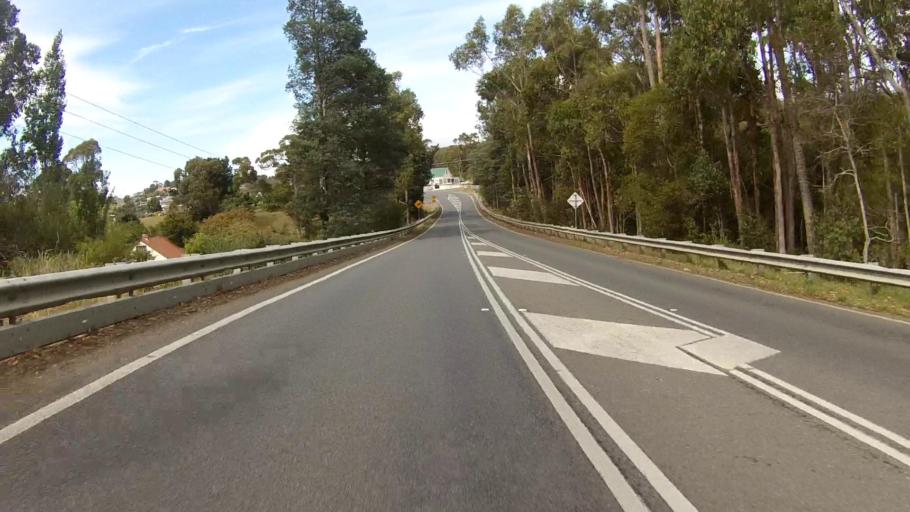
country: AU
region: Tasmania
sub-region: Kingborough
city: Kettering
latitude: -43.1213
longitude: 147.2462
